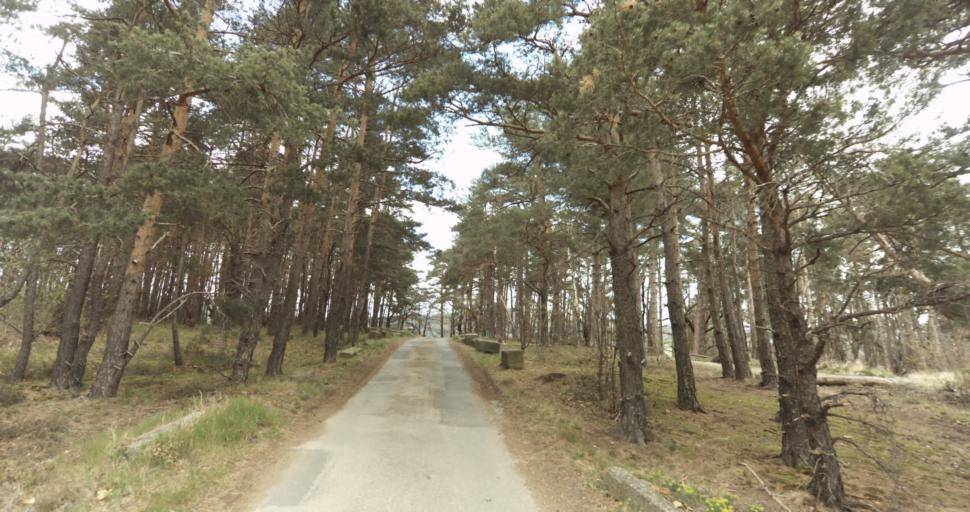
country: FR
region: Rhone-Alpes
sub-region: Departement de la Loire
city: Saint-Jean-Bonnefonds
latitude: 45.4469
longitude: 4.4606
